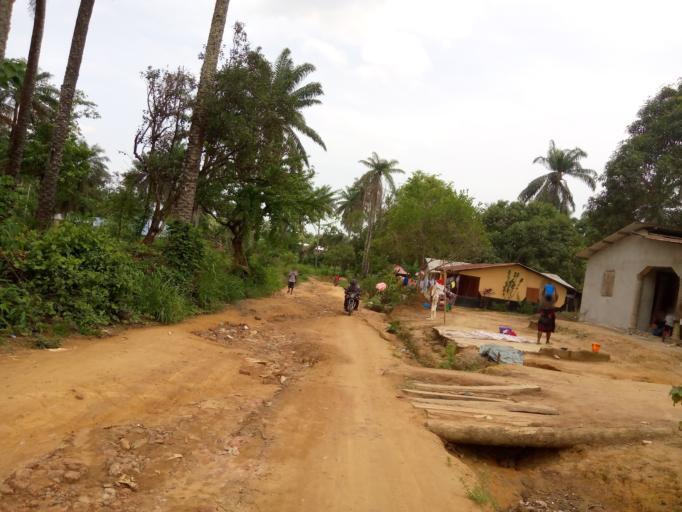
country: SL
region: Western Area
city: Waterloo
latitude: 8.3329
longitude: -13.0182
